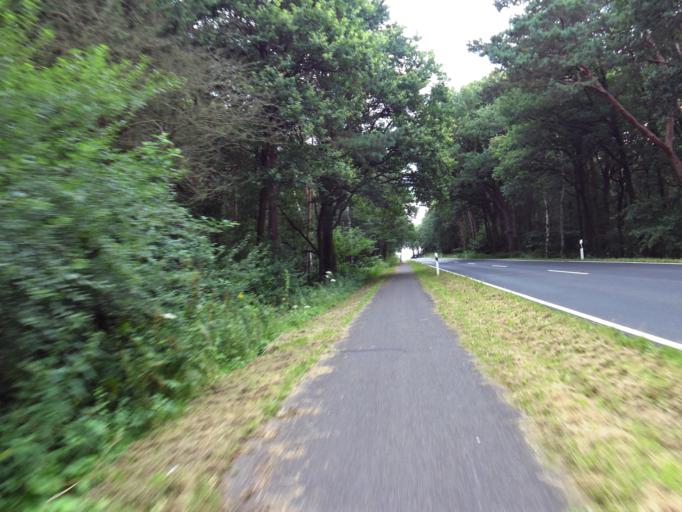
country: DE
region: North Rhine-Westphalia
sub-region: Regierungsbezirk Koln
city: Selfkant
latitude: 51.0075
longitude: 5.9337
